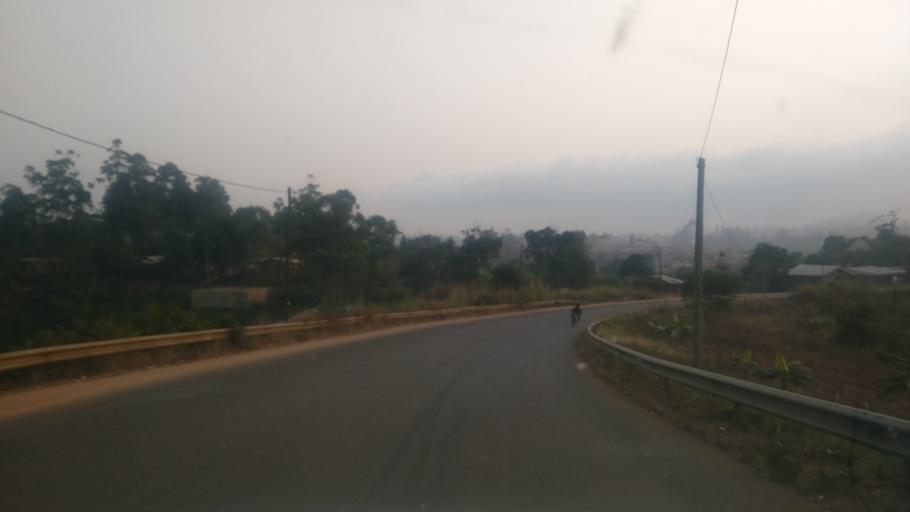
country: CM
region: West
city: Bana
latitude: 5.1396
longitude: 10.2950
